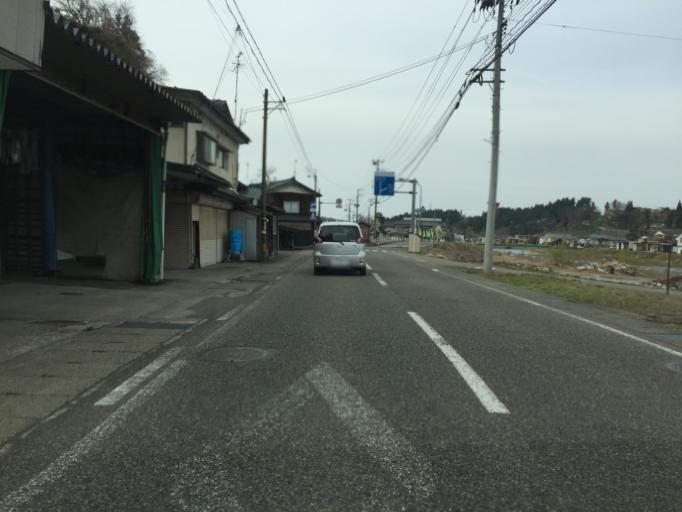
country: JP
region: Niigata
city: Tochio-honcho
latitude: 37.4652
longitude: 139.0045
